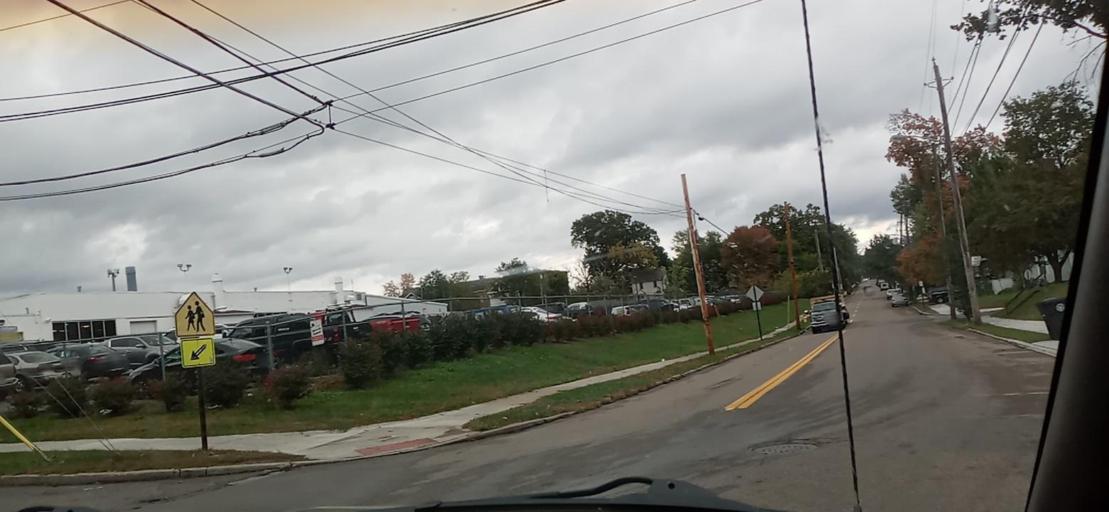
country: US
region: Ohio
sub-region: Summit County
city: Akron
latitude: 41.0891
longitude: -81.5300
